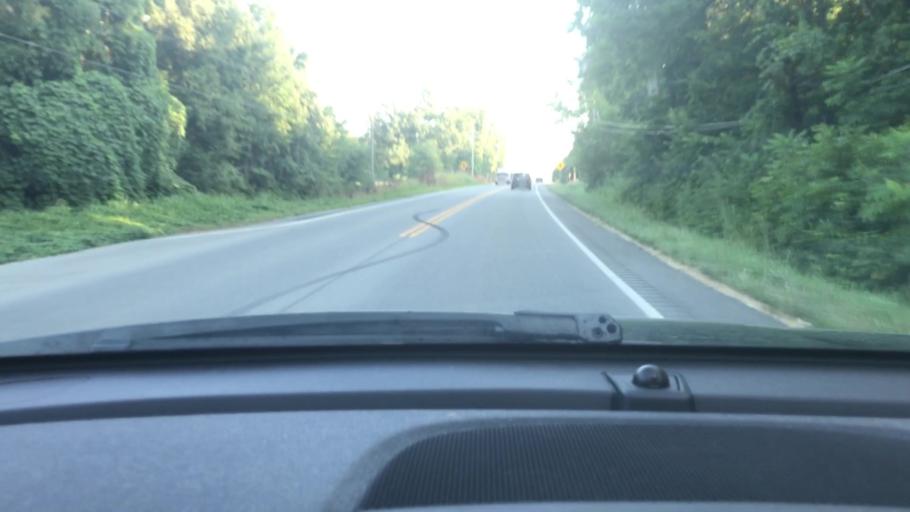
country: US
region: Tennessee
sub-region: Dickson County
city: Charlotte
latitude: 36.1528
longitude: -87.3560
